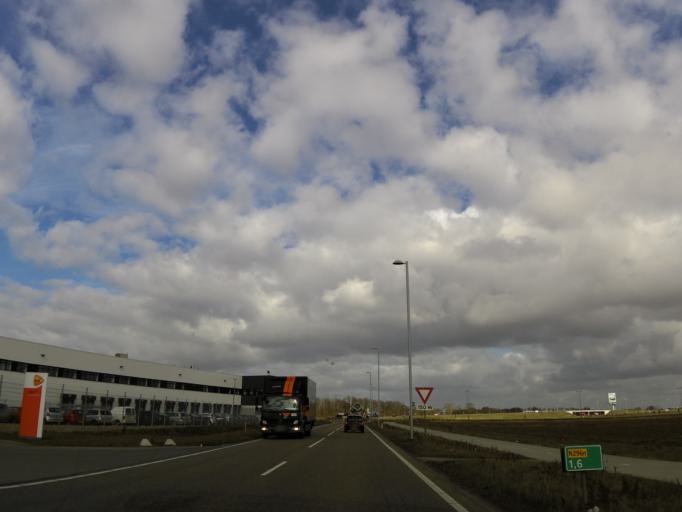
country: NL
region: Limburg
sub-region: Gemeente Sittard-Geleen
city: Born
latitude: 51.0681
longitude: 5.8192
